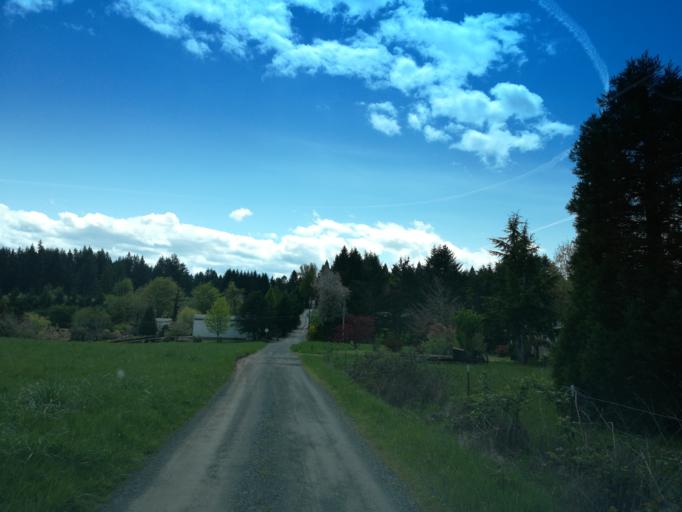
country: US
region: Oregon
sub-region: Clackamas County
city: Damascus
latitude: 45.4519
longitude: -122.4479
